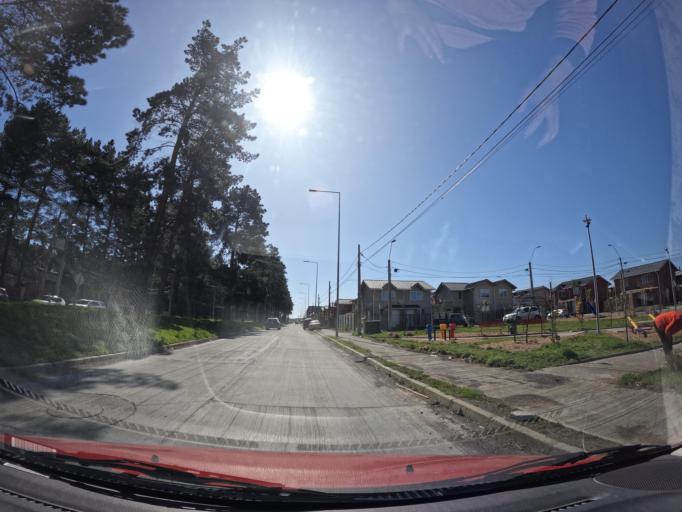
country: CL
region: Biobio
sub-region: Provincia de Concepcion
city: Concepcion
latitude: -36.8854
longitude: -73.1493
